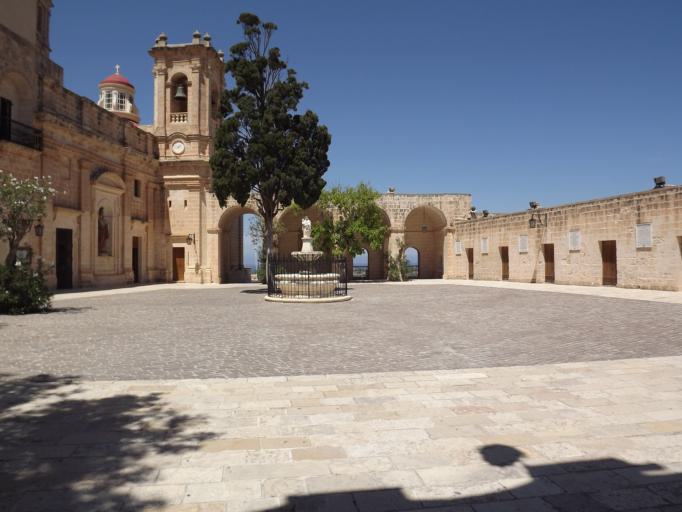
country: MT
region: Il-Mellieha
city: Mellieha
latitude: 35.9601
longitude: 14.3615
